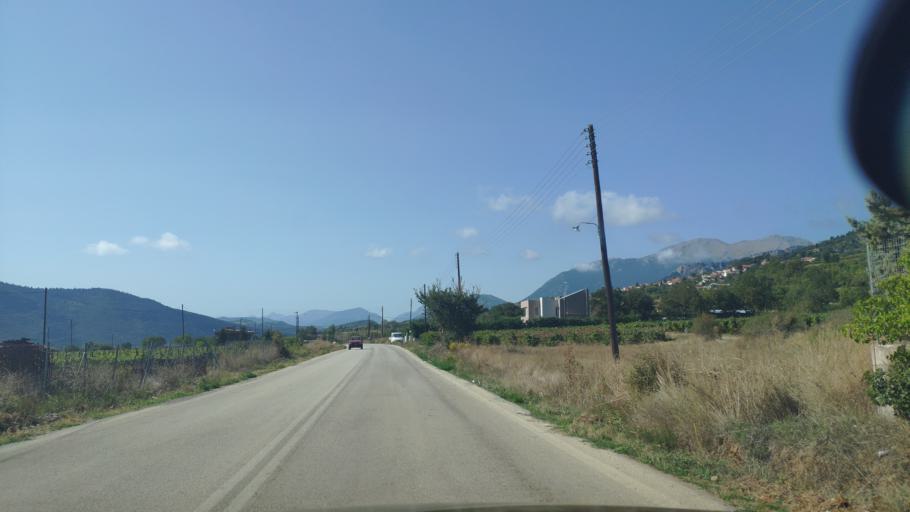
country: GR
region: Peloponnese
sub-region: Nomos Korinthias
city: Xylokastro
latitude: 37.9579
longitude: 22.5783
